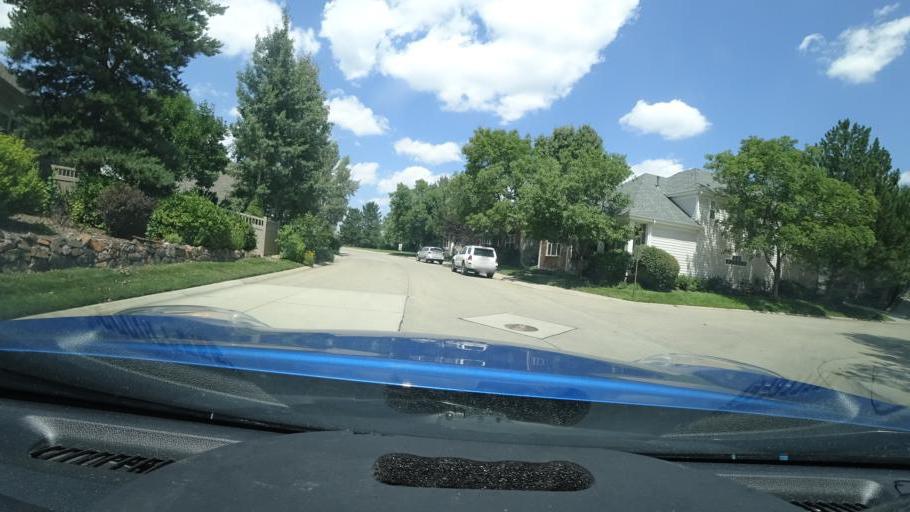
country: US
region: Colorado
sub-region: Arapahoe County
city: Glendale
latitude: 39.6992
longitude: -104.8943
